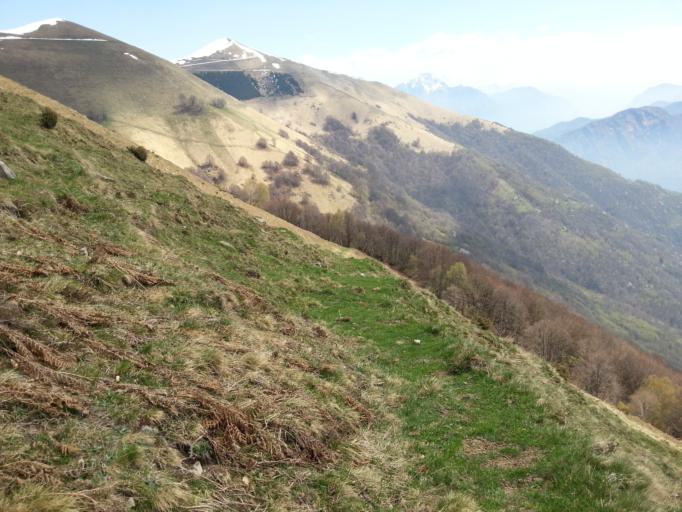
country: IT
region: Lombardy
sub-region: Provincia di Como
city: Bene Lario
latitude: 46.0050
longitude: 9.1556
